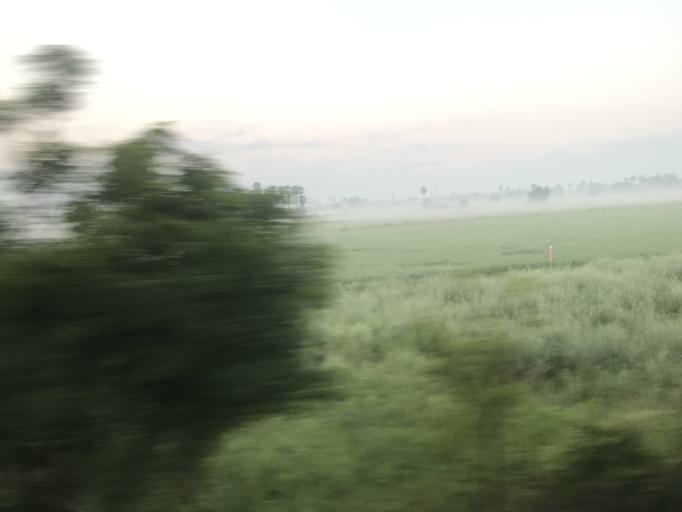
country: IN
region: Andhra Pradesh
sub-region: Guntur
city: Ponnur
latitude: 16.1017
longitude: 80.5727
